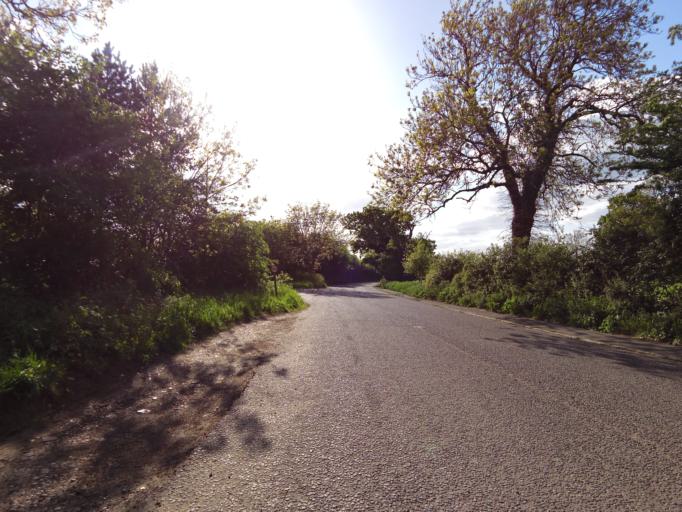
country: GB
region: England
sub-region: Suffolk
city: Beccles
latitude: 52.4468
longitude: 1.6175
